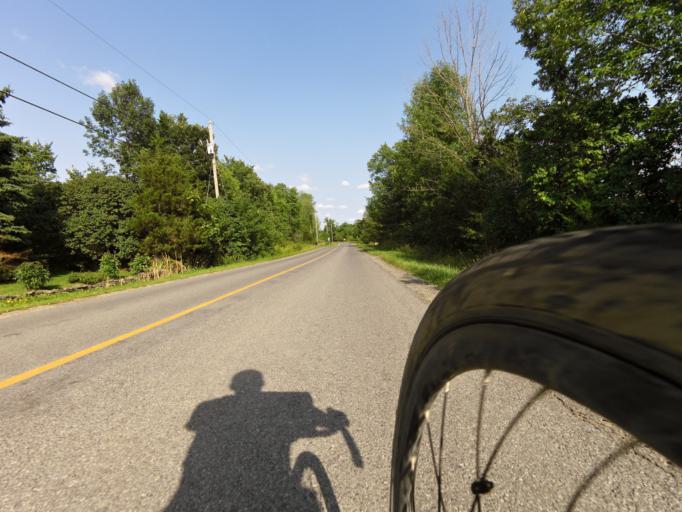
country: CA
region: Ontario
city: Kingston
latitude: 44.3692
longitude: -76.5972
